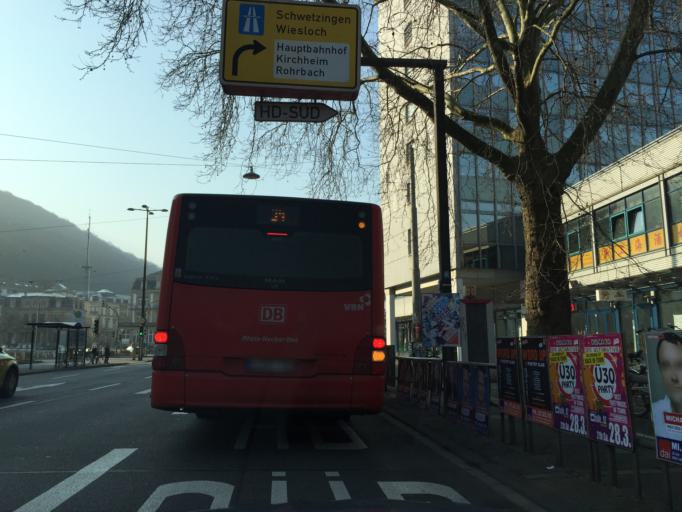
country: DE
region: Baden-Wuerttemberg
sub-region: Karlsruhe Region
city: Heidelberg
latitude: 49.4080
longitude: 8.6924
